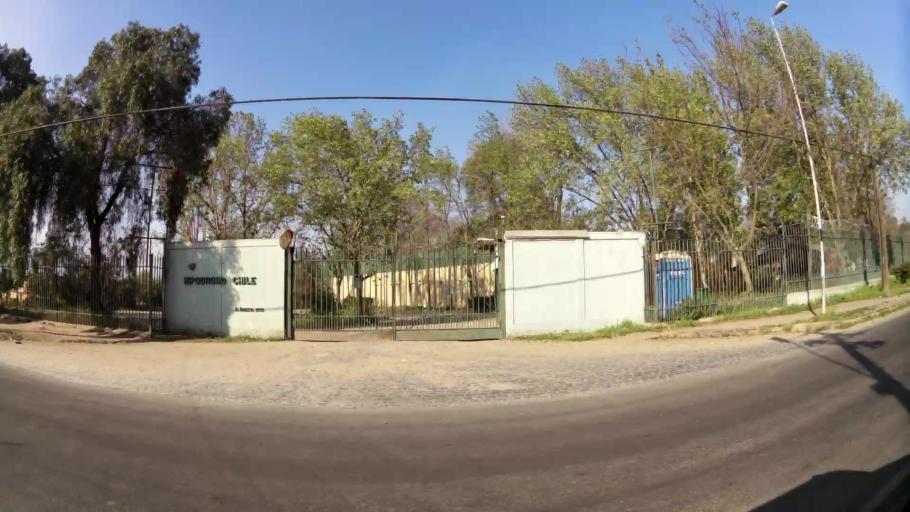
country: CL
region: Santiago Metropolitan
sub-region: Provincia de Santiago
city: Santiago
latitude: -33.4020
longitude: -70.6711
